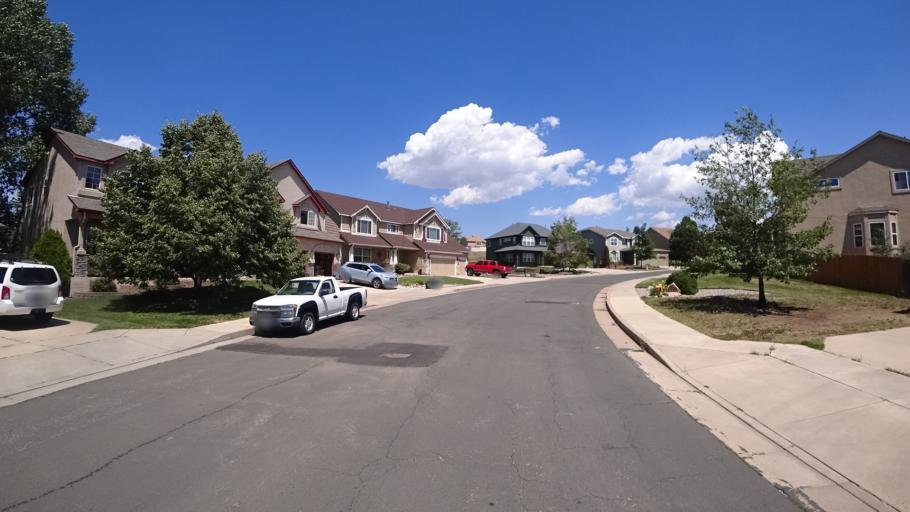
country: US
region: Colorado
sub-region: El Paso County
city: Black Forest
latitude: 38.9557
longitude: -104.7633
